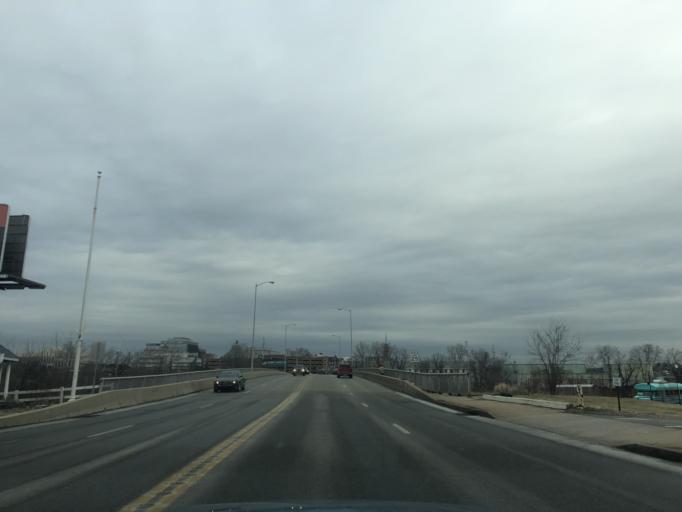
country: US
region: Pennsylvania
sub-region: Montgomery County
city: Bridgeport
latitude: 40.1085
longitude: -75.3450
